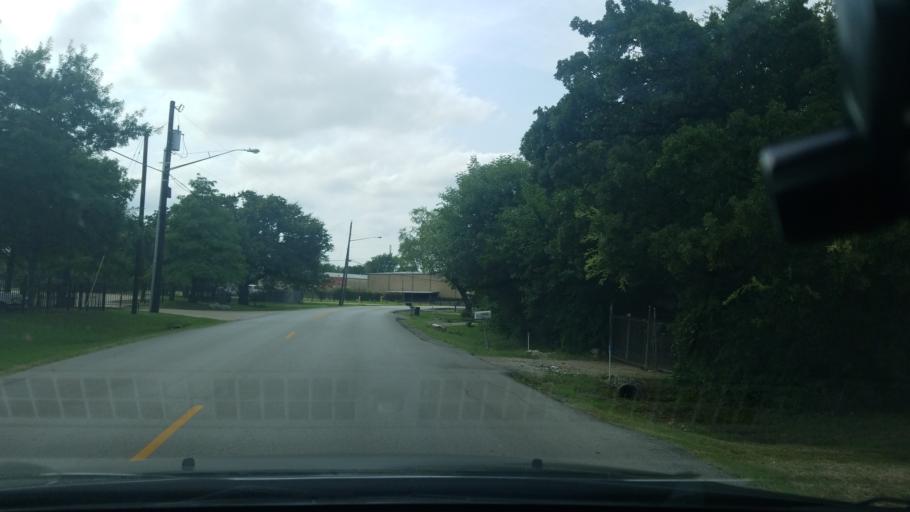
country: US
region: Texas
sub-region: Dallas County
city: Balch Springs
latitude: 32.7587
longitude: -96.6427
